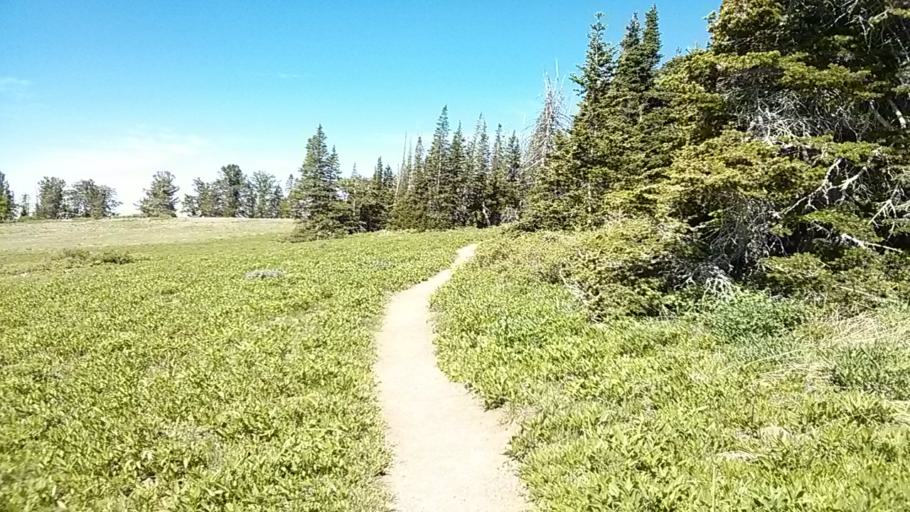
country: US
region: Utah
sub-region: Iron County
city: Parowan
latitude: 37.6333
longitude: -112.8302
